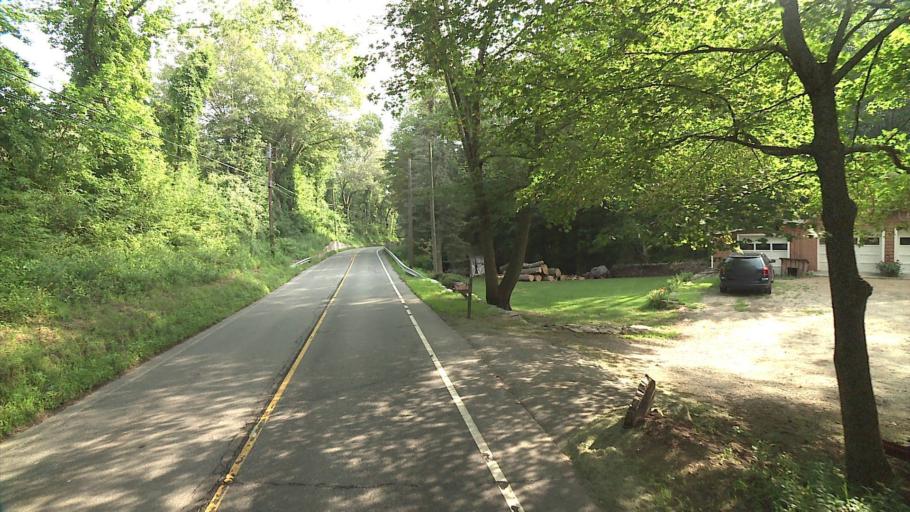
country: US
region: Connecticut
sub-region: Windham County
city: Quinebaug
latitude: 42.0160
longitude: -71.9638
